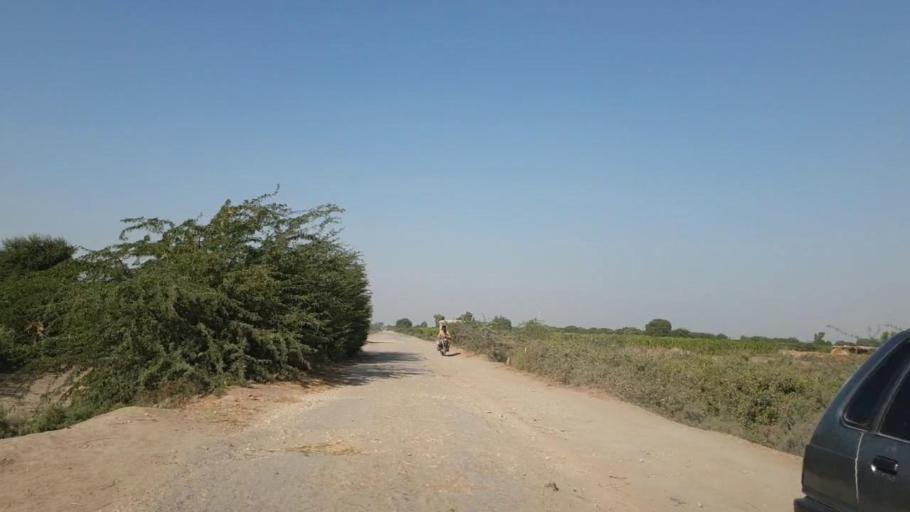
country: PK
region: Sindh
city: Digri
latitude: 25.0374
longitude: 69.1048
